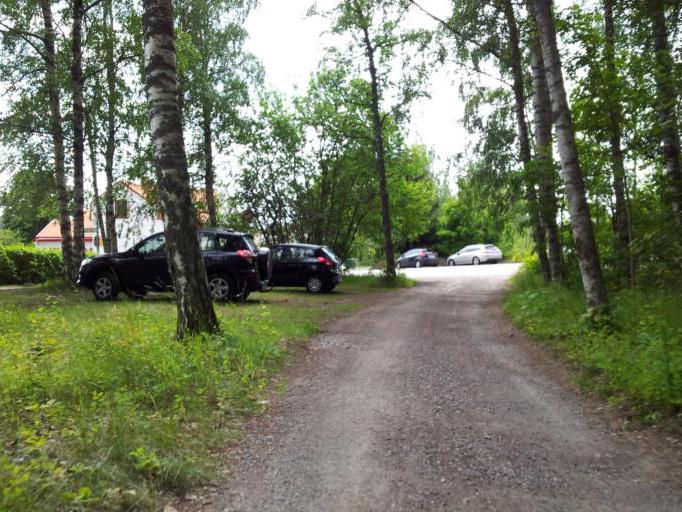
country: SE
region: Uppsala
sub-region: Uppsala Kommun
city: Saevja
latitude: 59.7884
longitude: 17.6616
